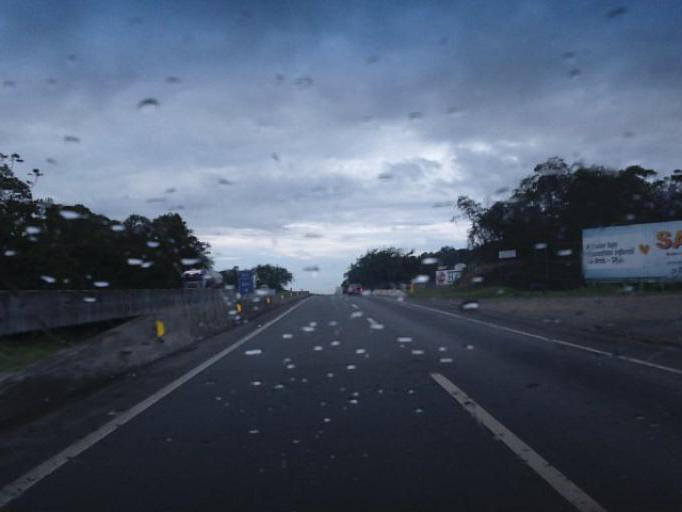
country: BR
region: Santa Catarina
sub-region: Joinville
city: Joinville
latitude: -26.0092
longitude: -48.8644
